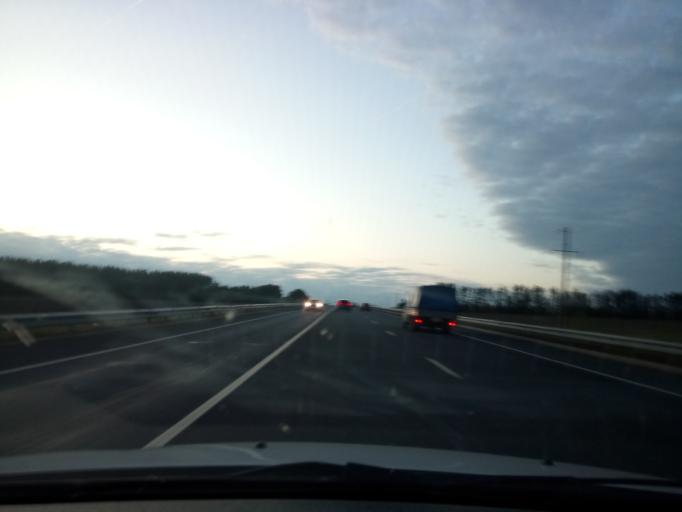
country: RU
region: Nizjnij Novgorod
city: Bol'shoye Murashkino
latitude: 55.8924
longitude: 44.7391
